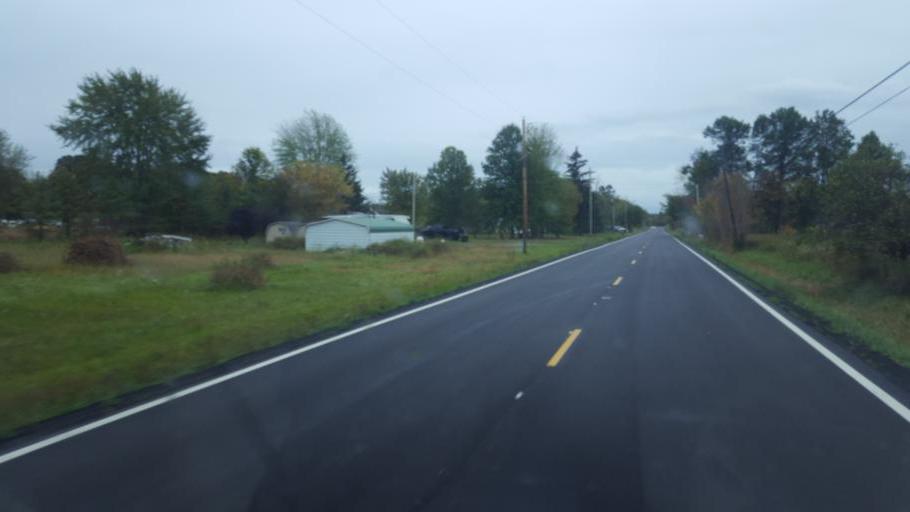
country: US
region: Ohio
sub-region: Huron County
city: New London
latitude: 41.0183
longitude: -82.3871
